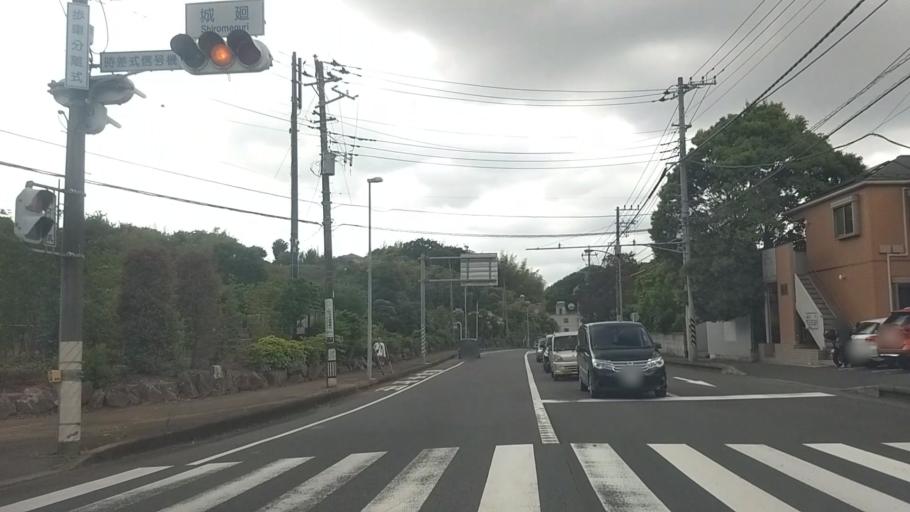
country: JP
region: Kanagawa
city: Fujisawa
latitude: 35.3574
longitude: 139.5162
